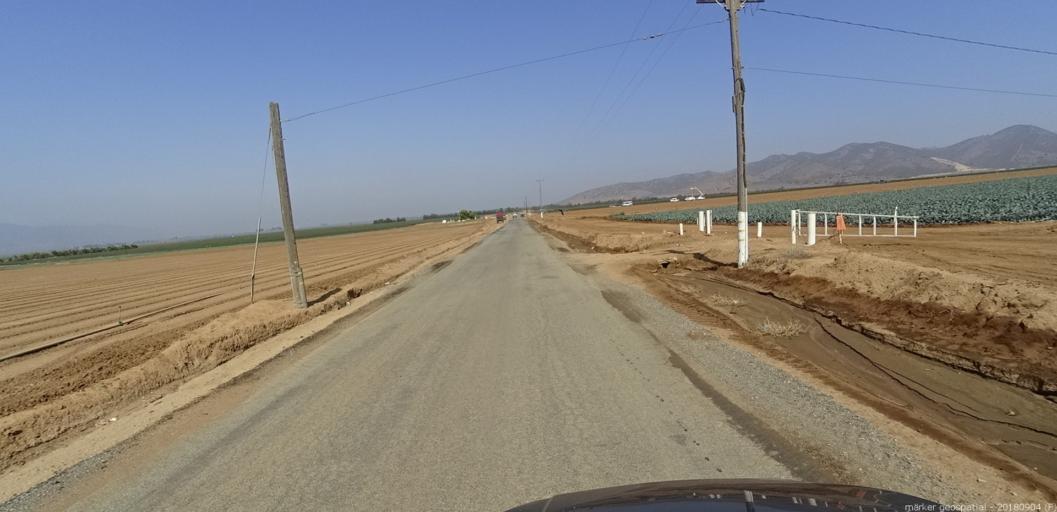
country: US
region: California
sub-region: Monterey County
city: Gonzales
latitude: 36.5408
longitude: -121.4275
